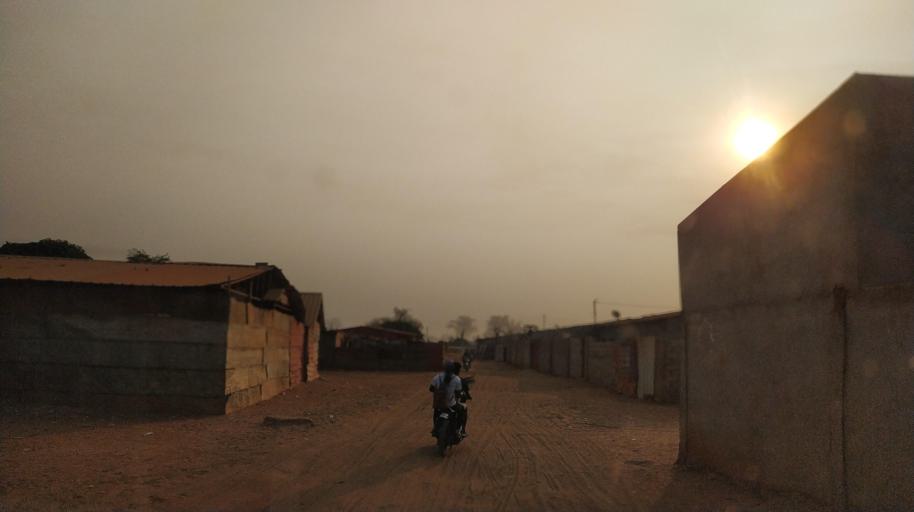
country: AO
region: Luanda
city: Luanda
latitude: -9.0728
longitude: 13.4206
